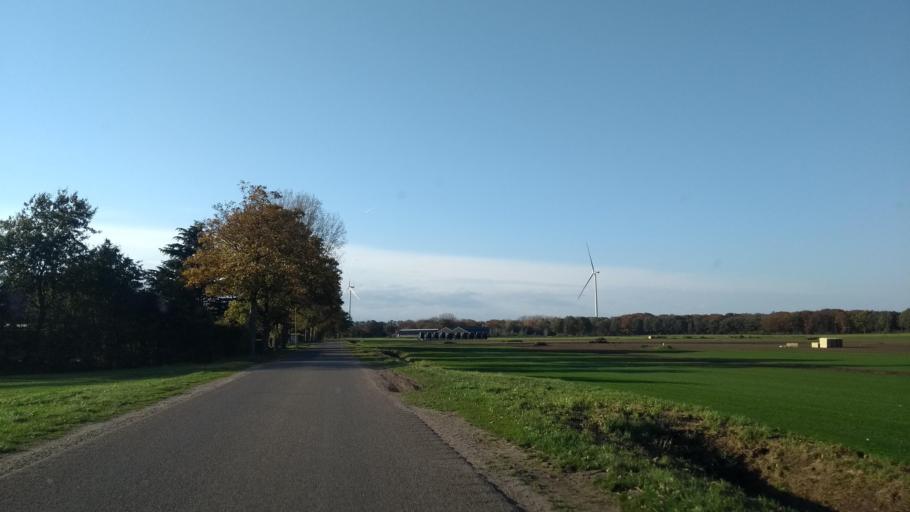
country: NL
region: Limburg
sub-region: Gemeente Leudal
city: Heythuysen
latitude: 51.3008
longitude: 5.8603
